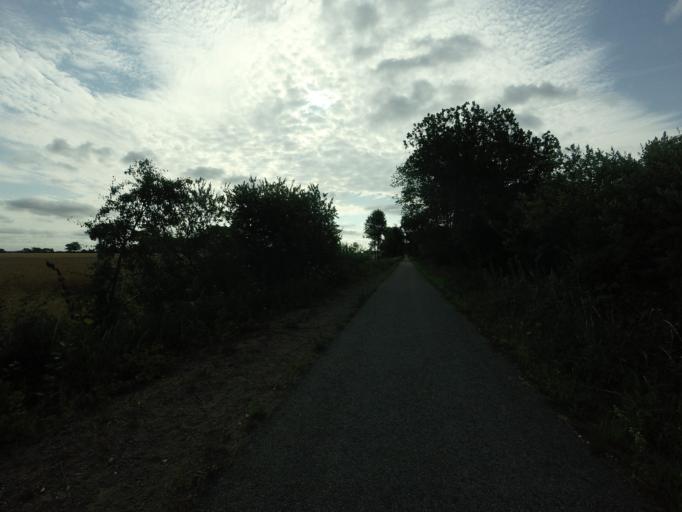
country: SE
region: Skane
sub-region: Hoganas Kommun
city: Hoganas
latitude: 56.1820
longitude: 12.6547
